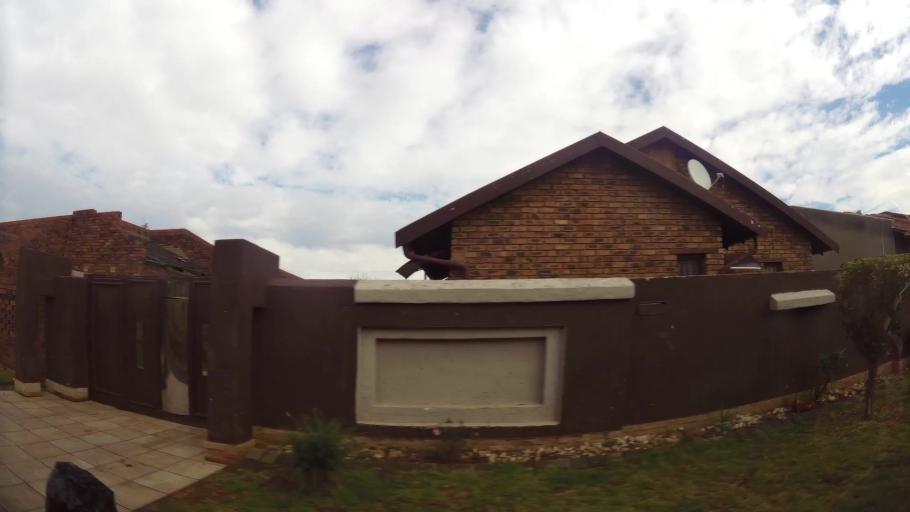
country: ZA
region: Gauteng
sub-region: Ekurhuleni Metropolitan Municipality
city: Germiston
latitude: -26.3208
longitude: 28.1785
